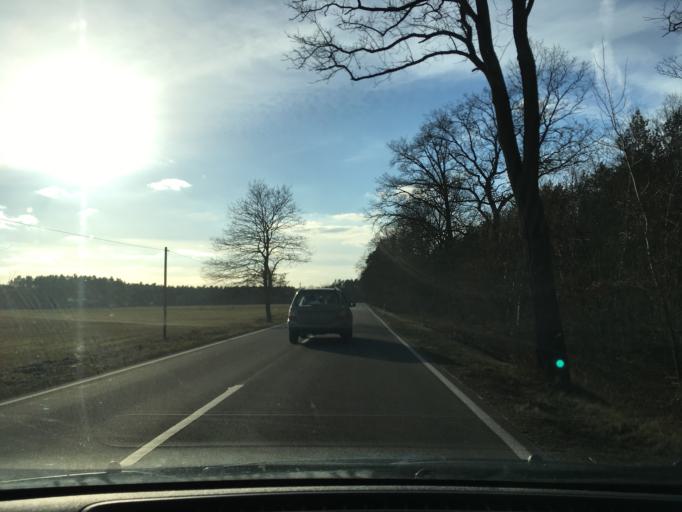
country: DE
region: Saxony-Anhalt
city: Seehausen
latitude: 52.8903
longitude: 11.6694
